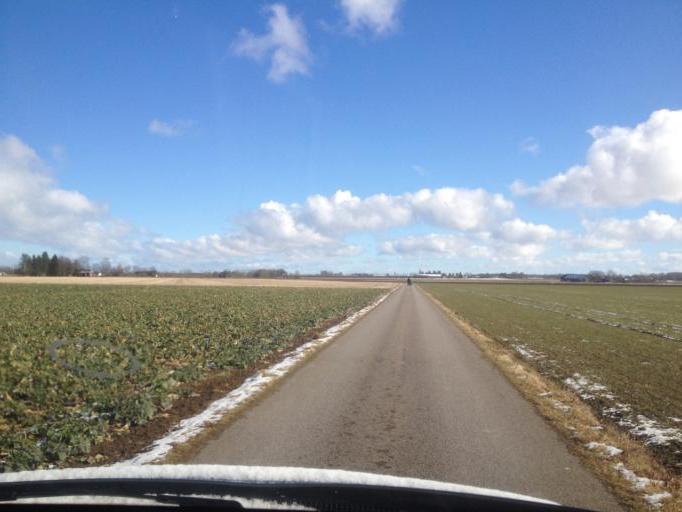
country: SE
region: OEstergoetland
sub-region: Mjolby Kommun
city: Mantorp
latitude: 58.4477
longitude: 15.3354
